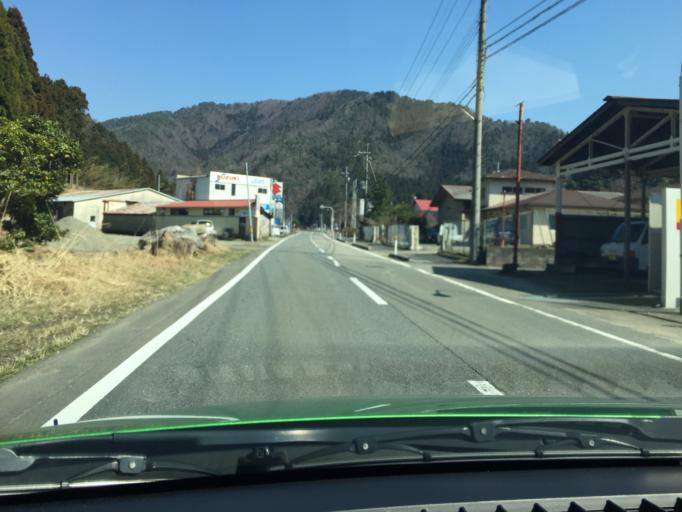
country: JP
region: Kyoto
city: Maizuru
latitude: 35.3171
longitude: 135.5566
